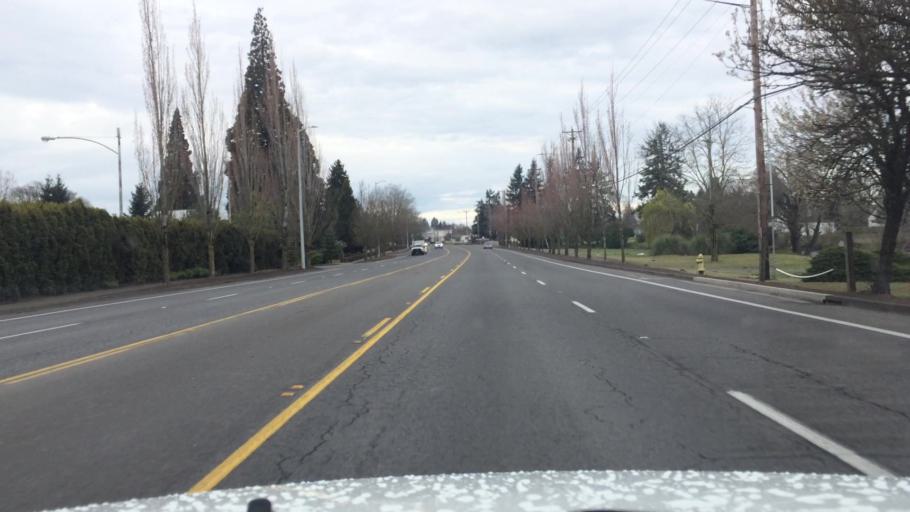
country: US
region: Oregon
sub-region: Marion County
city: Four Corners
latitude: 44.9298
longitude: -123.0047
